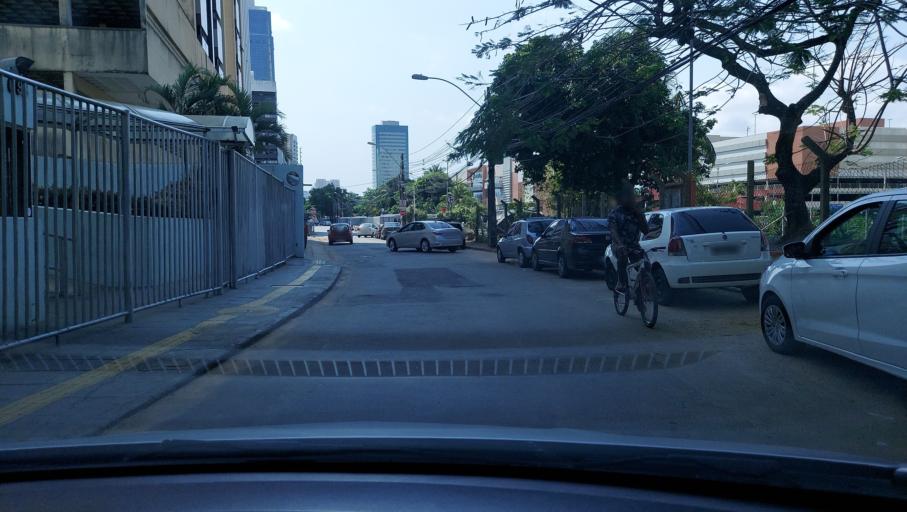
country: BR
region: Bahia
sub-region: Salvador
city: Salvador
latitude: -12.9816
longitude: -38.4529
